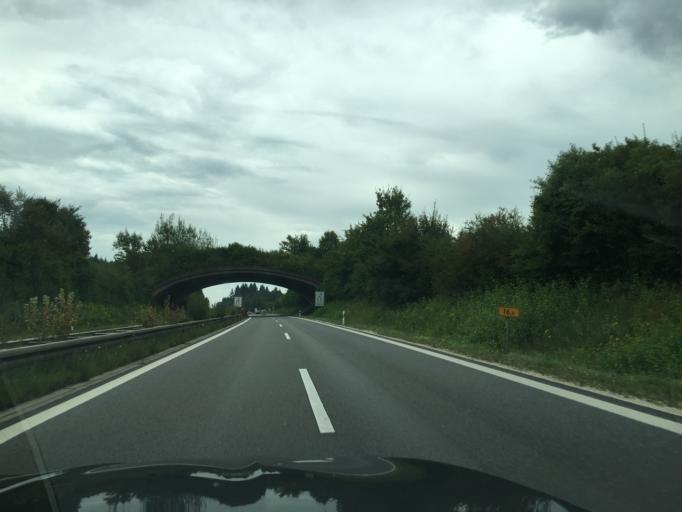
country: DE
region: Baden-Wuerttemberg
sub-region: Freiburg Region
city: Radolfzell am Bodensee
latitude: 47.7396
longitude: 9.0180
